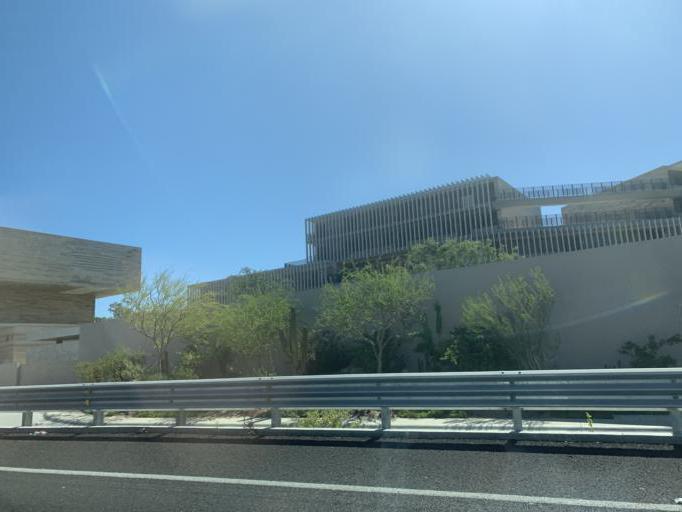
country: MX
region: Baja California Sur
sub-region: Los Cabos
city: San Jose del Cabo
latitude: 22.9737
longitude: -109.7832
